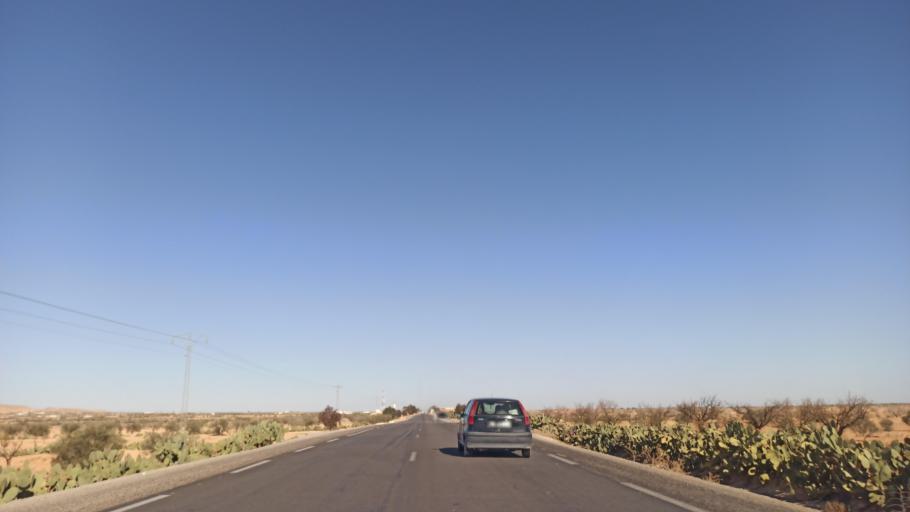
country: TN
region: Sidi Bu Zayd
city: Bi'r al Hufayy
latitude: 34.7326
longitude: 9.0683
